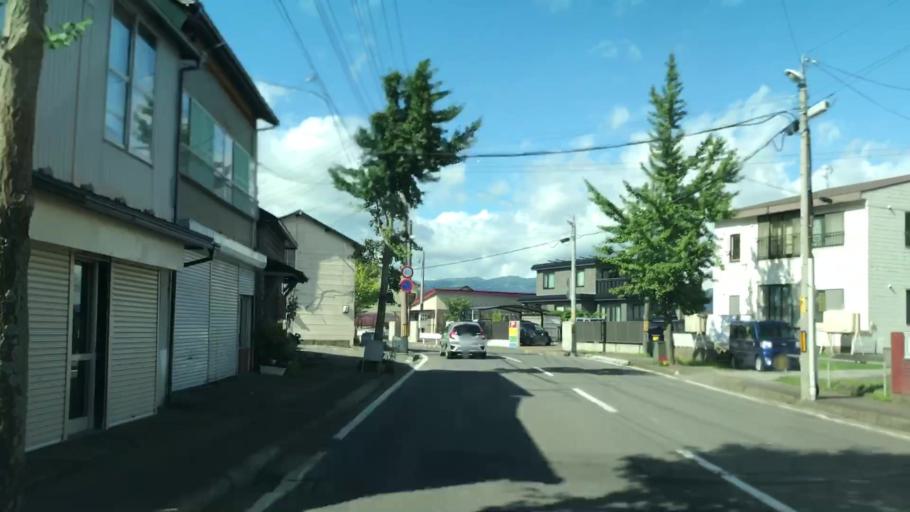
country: JP
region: Hokkaido
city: Muroran
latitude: 42.3245
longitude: 140.9677
